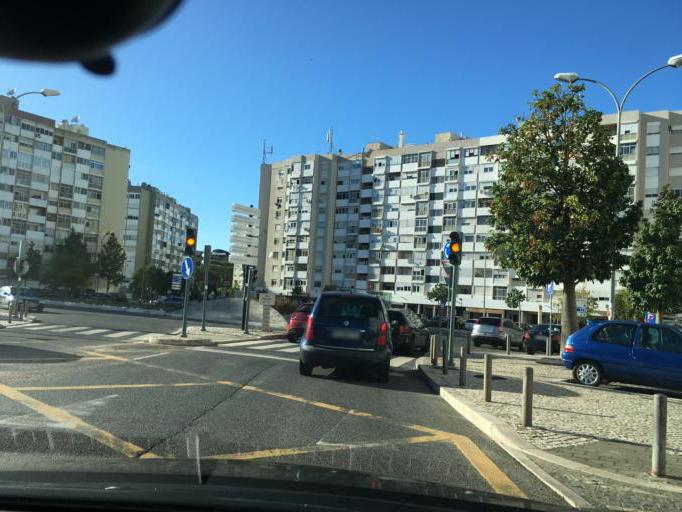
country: PT
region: Lisbon
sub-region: Odivelas
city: Pontinha
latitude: 38.7603
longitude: -9.2037
